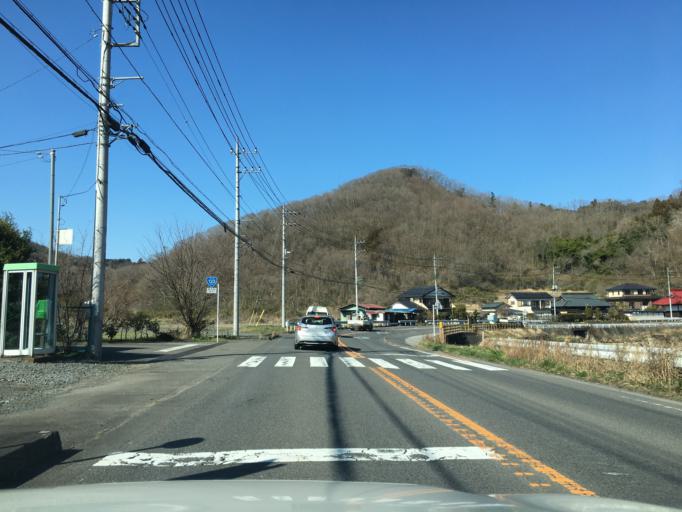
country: JP
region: Tochigi
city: Motegi
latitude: 36.5476
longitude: 140.2217
